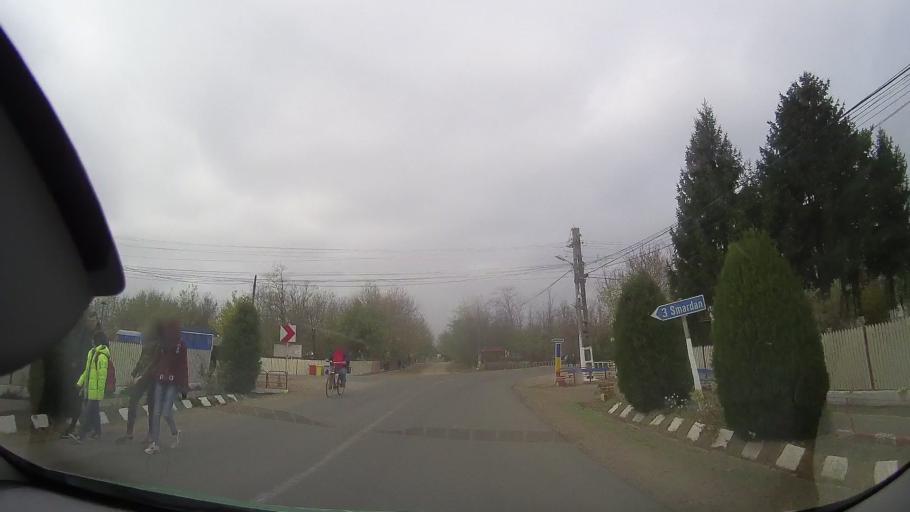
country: RO
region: Buzau
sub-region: Comuna Scutelnici
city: Scutelnici
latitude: 44.8794
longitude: 26.8772
